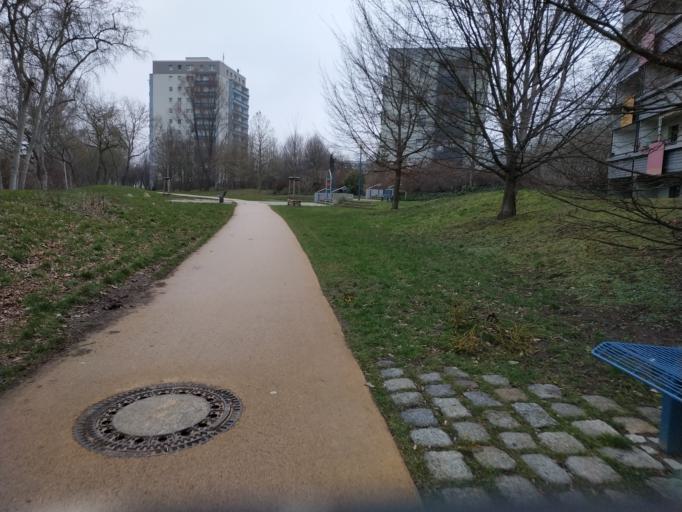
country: DE
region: Berlin
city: Marzahn
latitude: 52.5378
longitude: 13.5858
